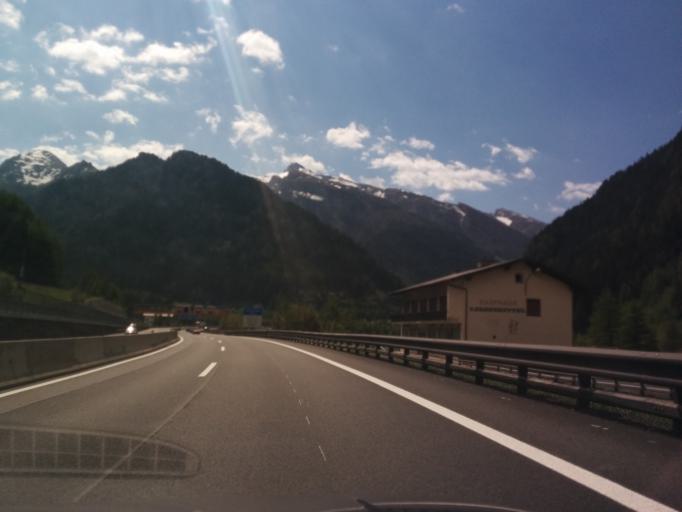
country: AT
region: Tyrol
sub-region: Politischer Bezirk Innsbruck Land
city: Gries am Brenner
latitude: 47.0208
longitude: 11.5028
